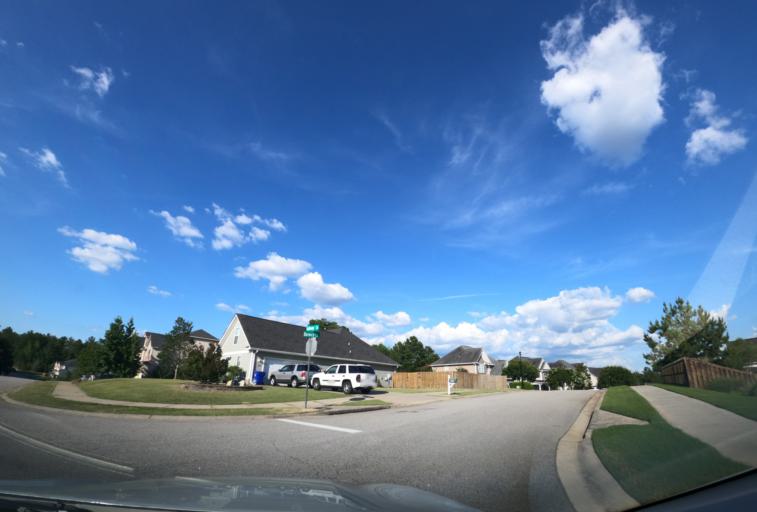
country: US
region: Georgia
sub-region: Columbia County
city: Grovetown
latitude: 33.5124
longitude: -82.2334
